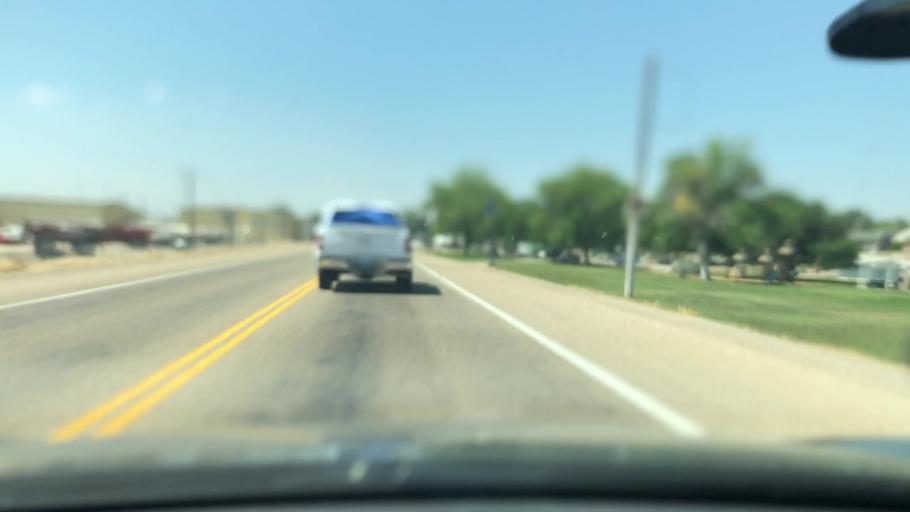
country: US
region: Idaho
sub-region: Canyon County
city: Parma
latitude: 43.7796
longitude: -116.9330
